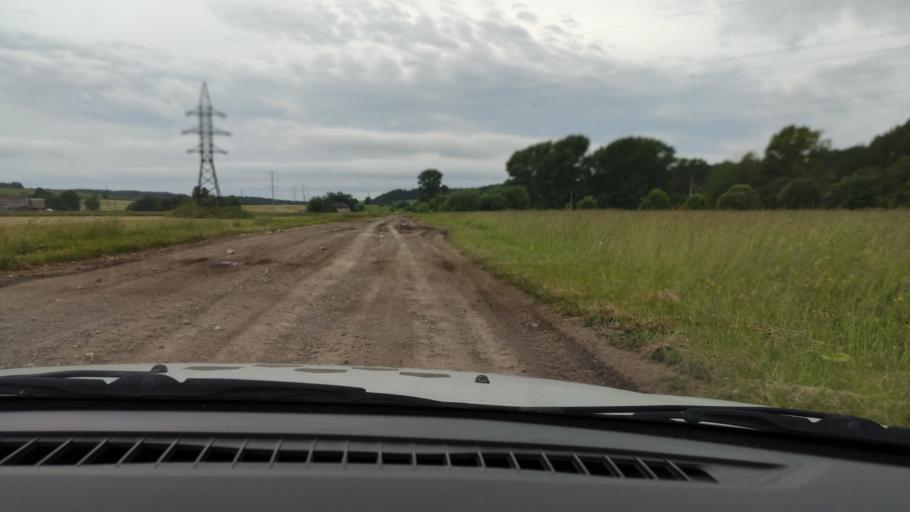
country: RU
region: Perm
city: Orda
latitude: 57.3005
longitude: 56.6224
